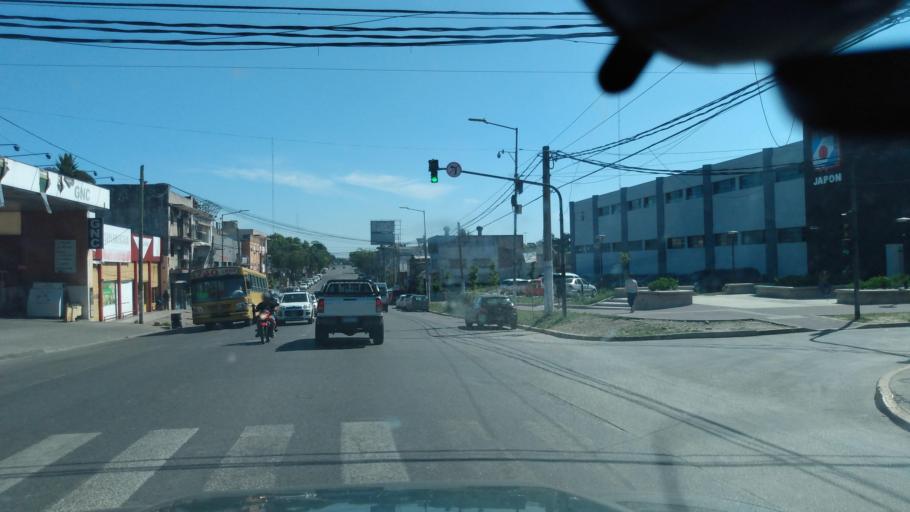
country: AR
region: Buenos Aires
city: Hurlingham
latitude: -34.5453
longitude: -58.7153
